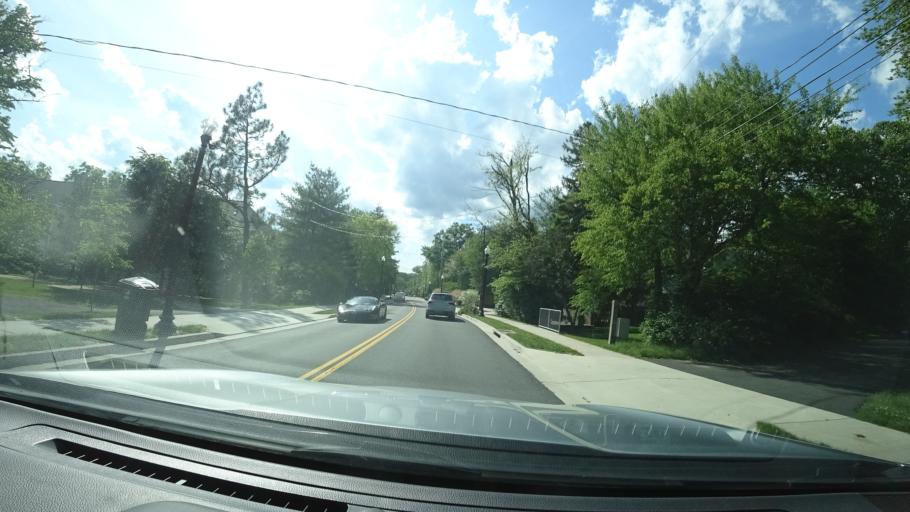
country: US
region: Maryland
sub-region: Montgomery County
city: Brookmont
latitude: 38.9092
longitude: -77.1346
